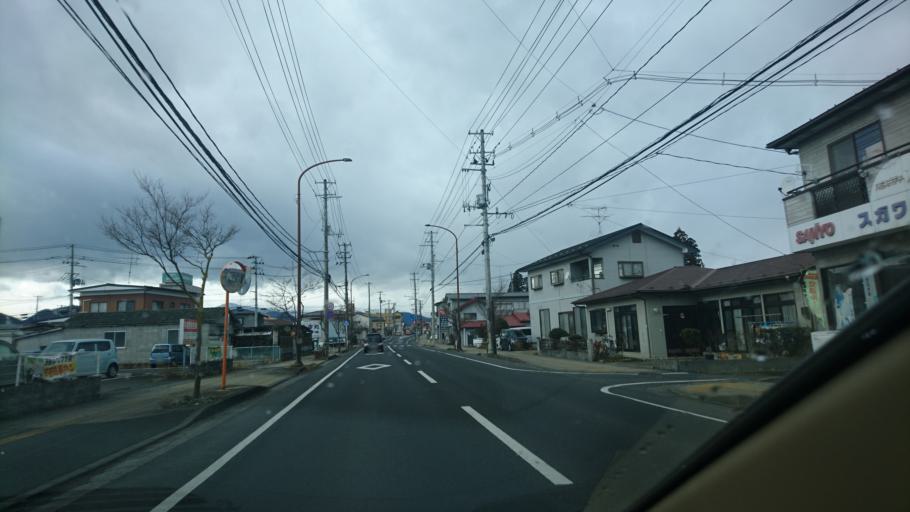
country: JP
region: Miyagi
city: Tomiya
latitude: 38.4427
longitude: 140.8952
